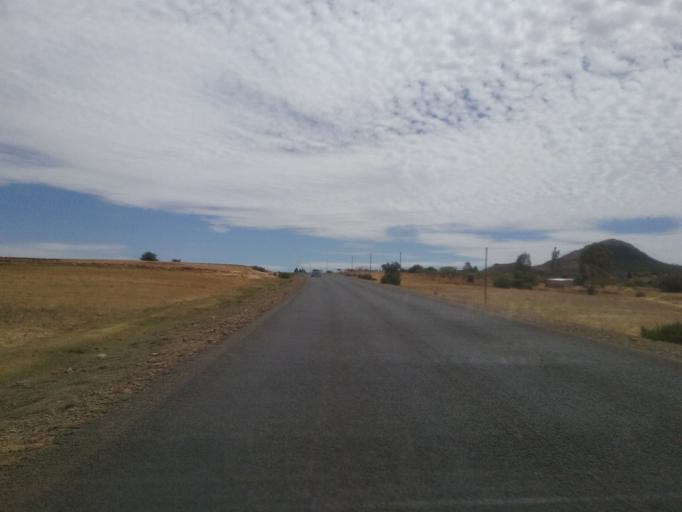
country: LS
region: Mafeteng
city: Mafeteng
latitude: -29.8629
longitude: 27.2360
